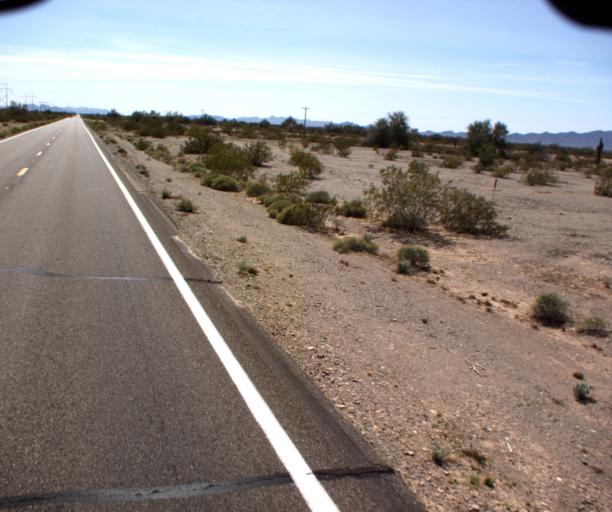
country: US
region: Arizona
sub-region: La Paz County
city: Quartzsite
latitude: 33.5165
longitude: -114.2170
